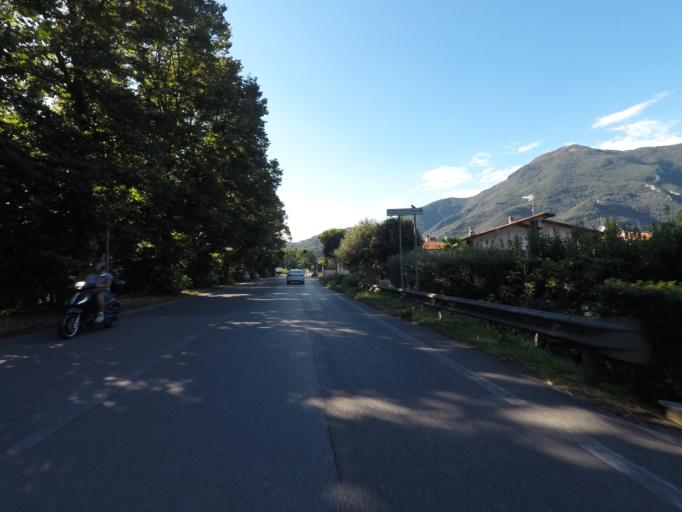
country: IT
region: Tuscany
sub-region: Provincia di Lucca
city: Corsanico-Bargecchia
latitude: 43.9337
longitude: 10.3078
